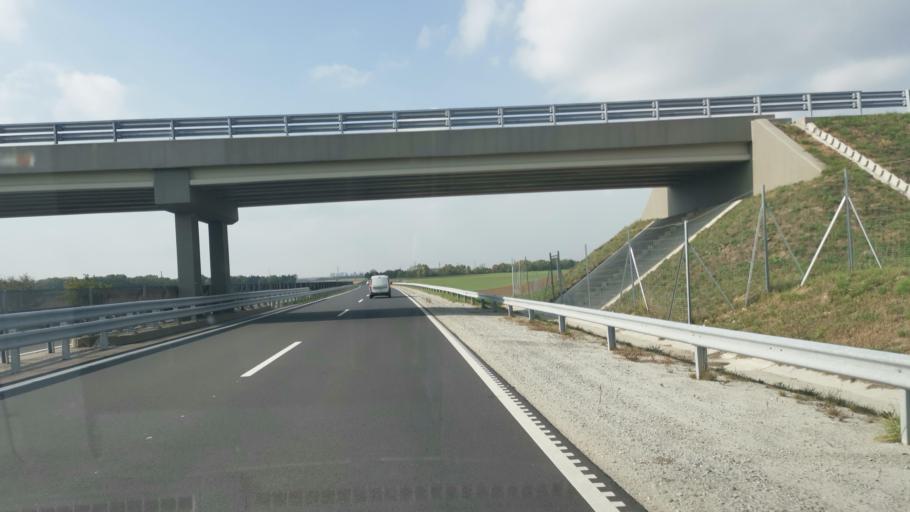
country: HU
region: Gyor-Moson-Sopron
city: Nagycenk
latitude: 47.5815
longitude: 16.7487
